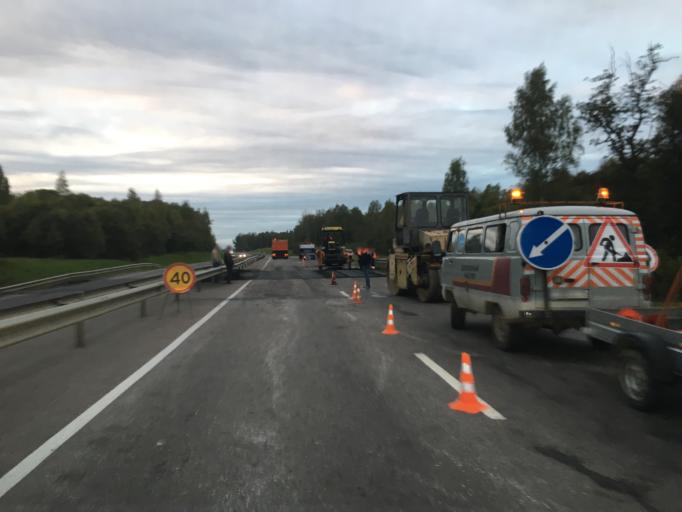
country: RU
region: Kaluga
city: Kaluga
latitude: 54.6066
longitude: 36.3133
